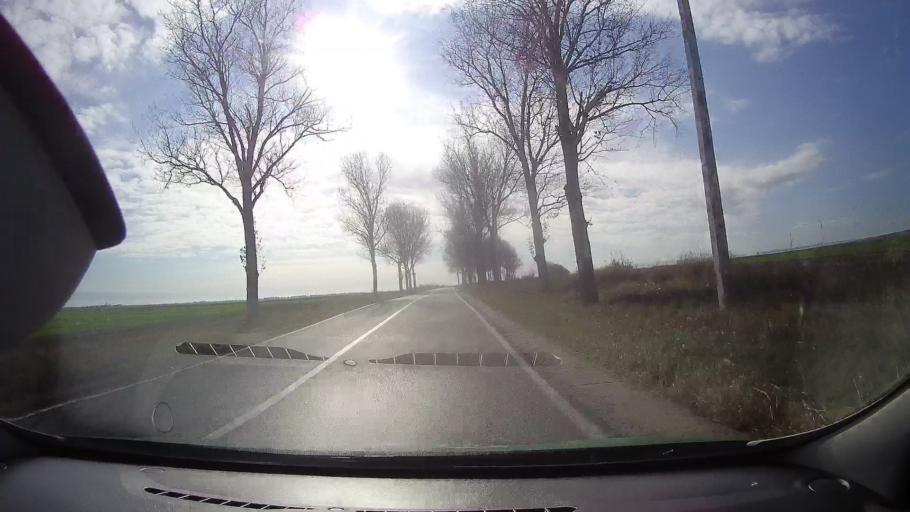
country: RO
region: Tulcea
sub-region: Comuna Valea Nucarilor
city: Agighiol
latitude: 44.9979
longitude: 28.8864
